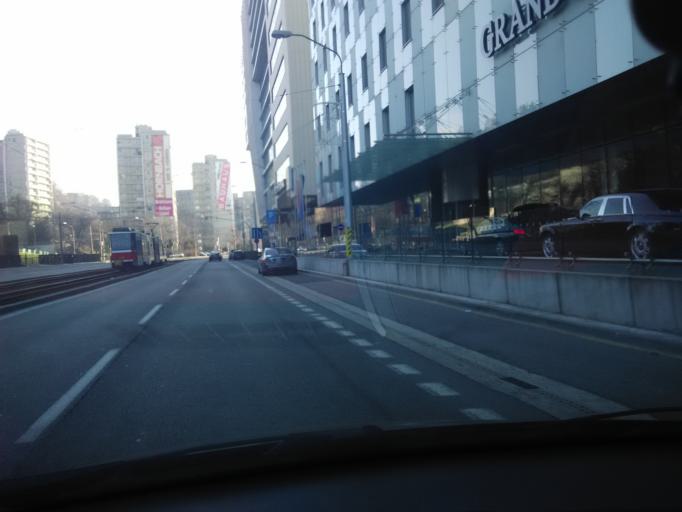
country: SK
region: Bratislavsky
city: Bratislava
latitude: 48.1419
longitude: 17.0896
